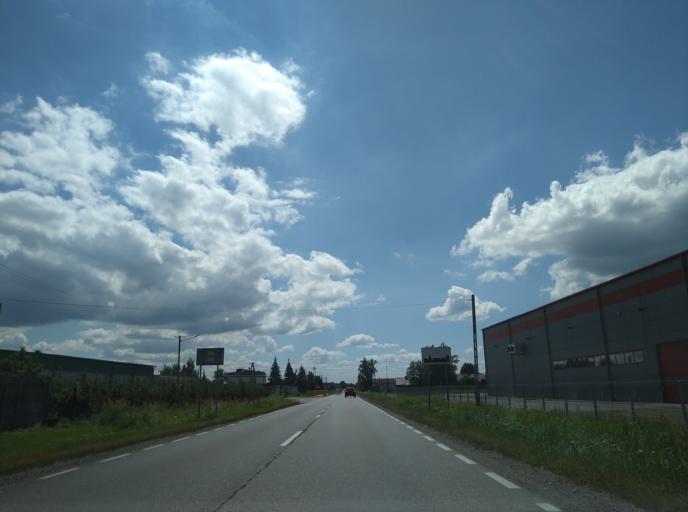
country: PL
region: Masovian Voivodeship
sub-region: Powiat piaseczynski
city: Gora Kalwaria
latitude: 51.8797
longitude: 21.2194
